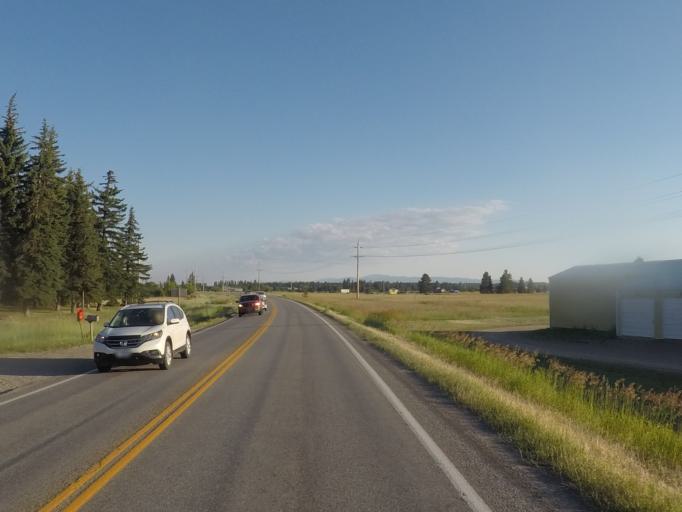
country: US
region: Montana
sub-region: Flathead County
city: Columbia Falls
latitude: 48.3554
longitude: -114.1588
